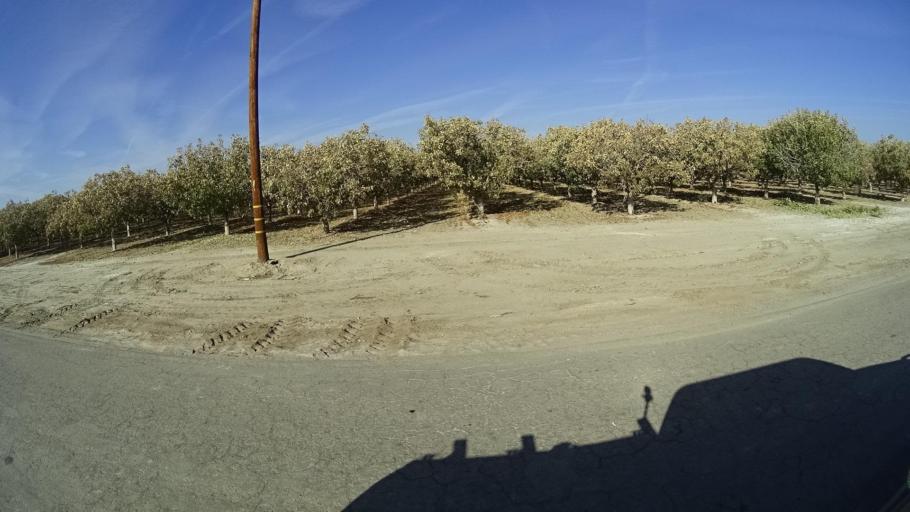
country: US
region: California
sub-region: Kern County
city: Wasco
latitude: 35.6886
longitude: -119.4264
